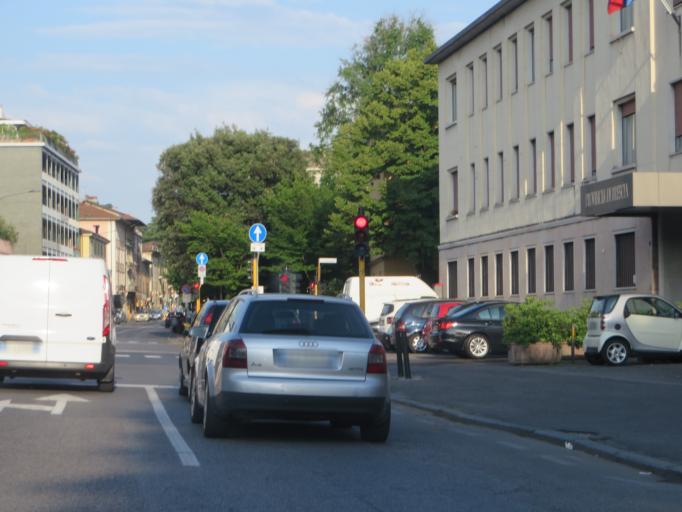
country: IT
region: Lombardy
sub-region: Provincia di Brescia
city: Brescia
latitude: 45.5433
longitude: 10.2049
